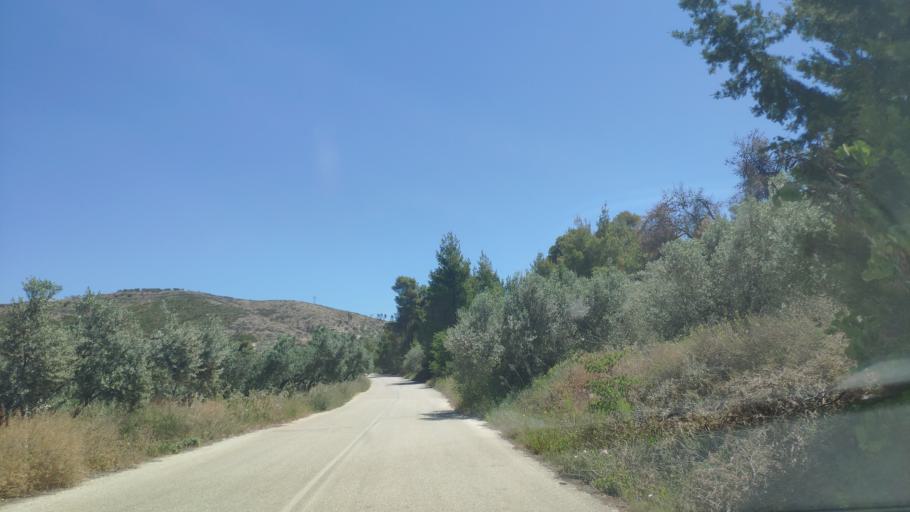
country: GR
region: Peloponnese
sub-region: Nomos Korinthias
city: Athikia
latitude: 37.8344
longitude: 22.9304
